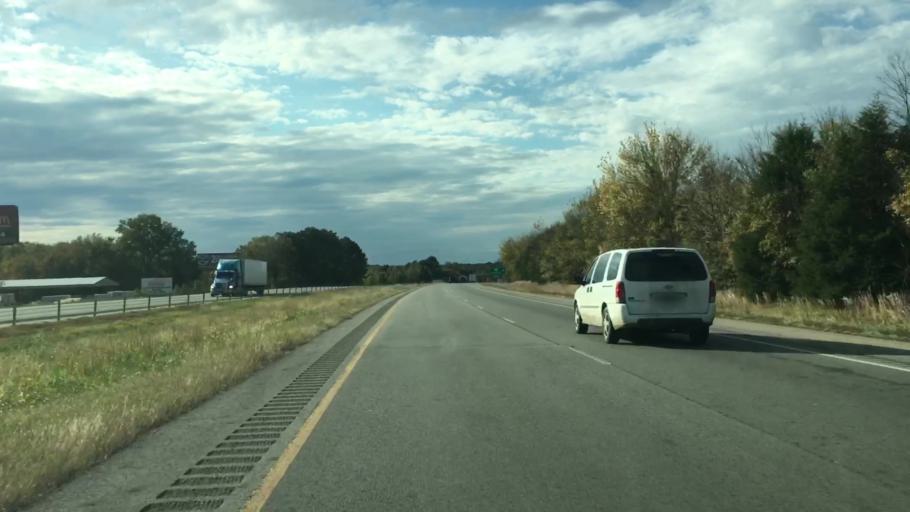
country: US
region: Arkansas
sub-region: Pope County
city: Pottsville
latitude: 35.2484
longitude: -93.0282
